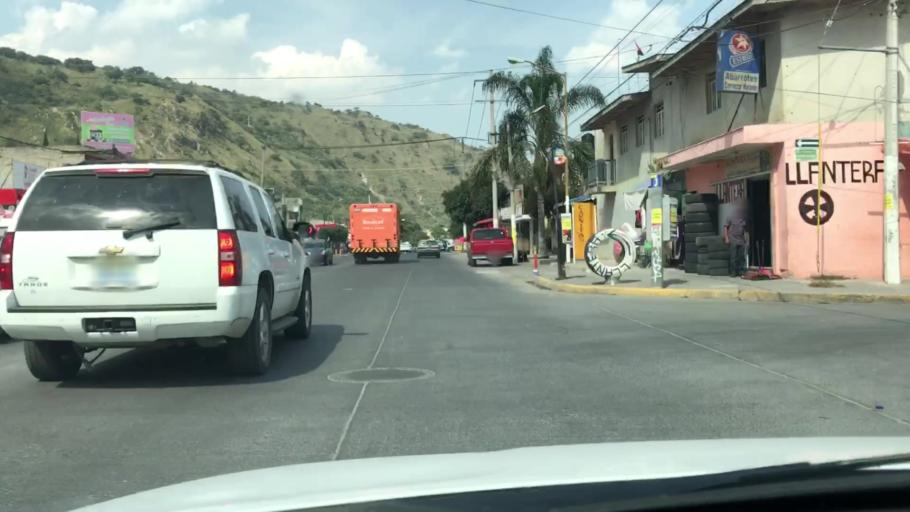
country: MX
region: Jalisco
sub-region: Tlajomulco de Zuniga
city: Palomar
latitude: 20.6443
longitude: -103.4604
